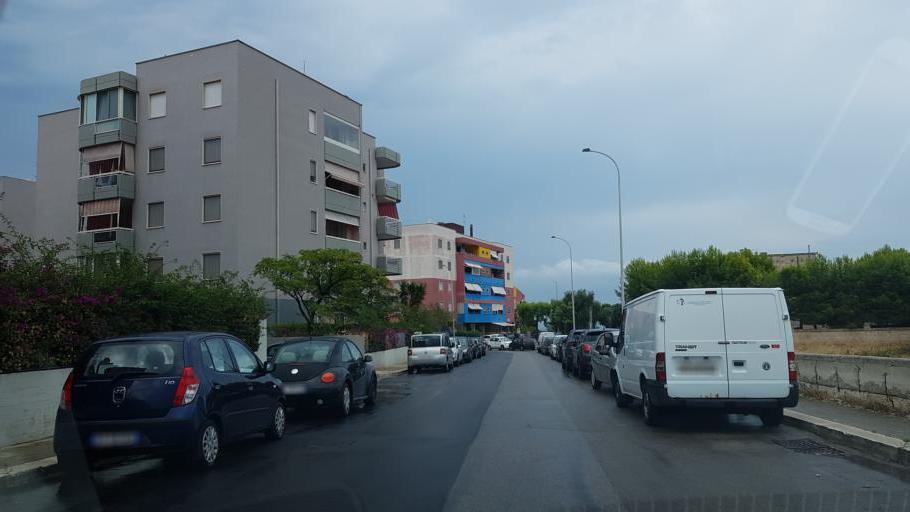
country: IT
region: Apulia
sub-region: Provincia di Bari
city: Monopoli
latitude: 40.9432
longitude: 17.3084
